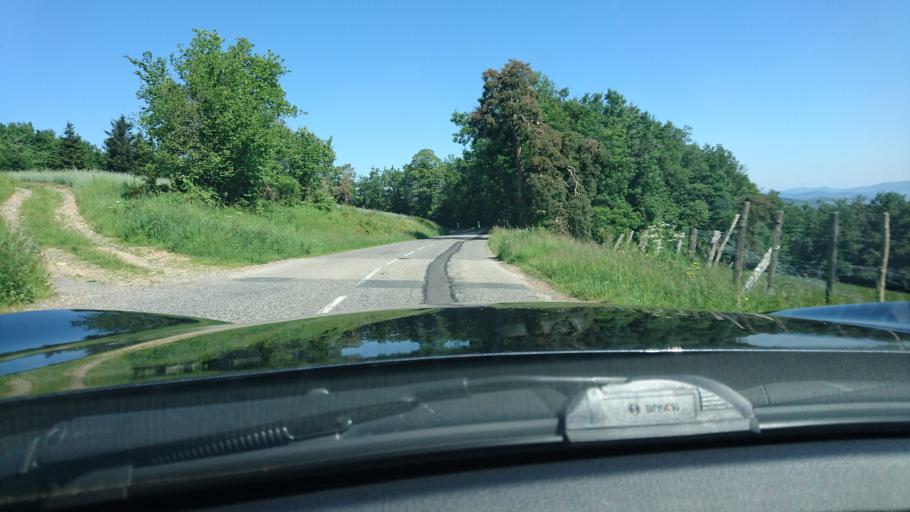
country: FR
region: Rhone-Alpes
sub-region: Departement du Rhone
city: Montrottier
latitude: 45.8012
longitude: 4.4333
